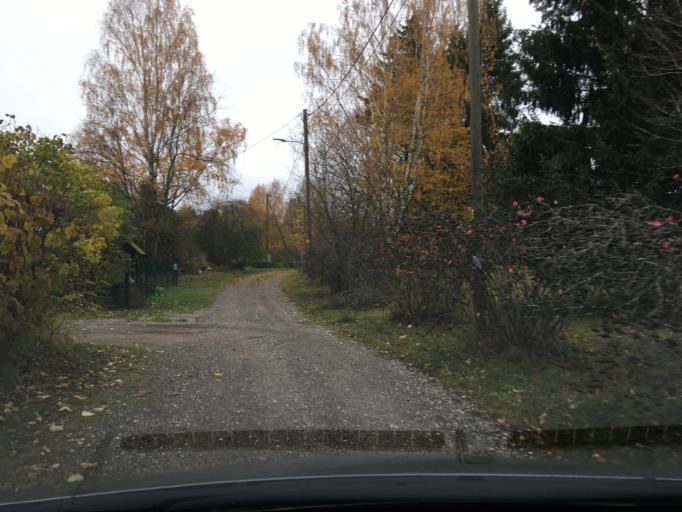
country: EE
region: Tartu
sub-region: UElenurme vald
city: Ulenurme
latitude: 58.3470
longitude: 26.7746
